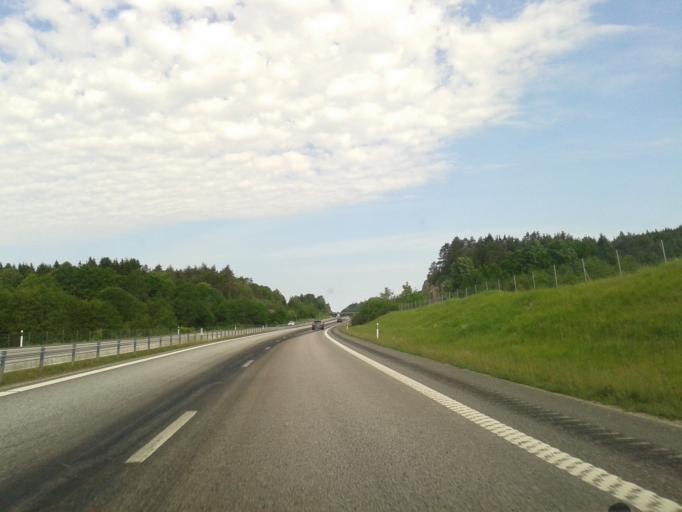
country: SE
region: Vaestra Goetaland
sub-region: Lysekils Kommun
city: Brastad
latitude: 58.5437
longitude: 11.5196
